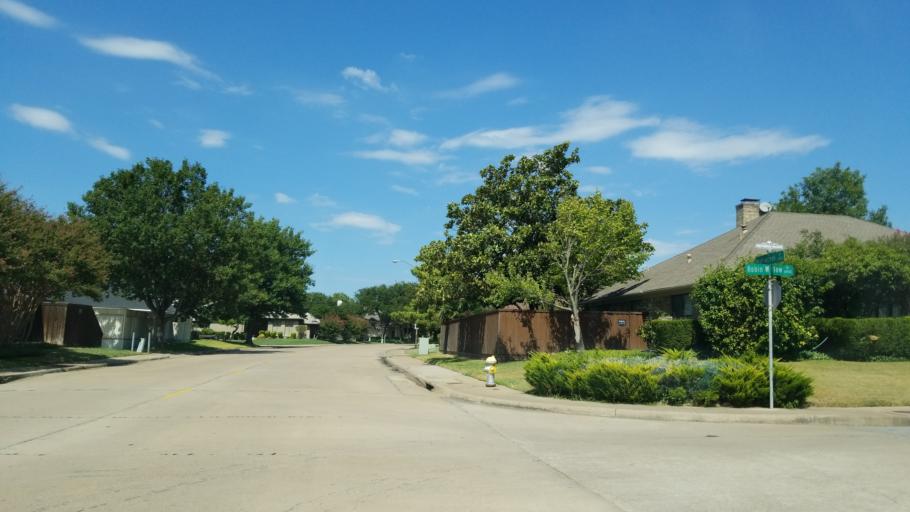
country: US
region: Texas
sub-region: Dallas County
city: Addison
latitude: 32.9686
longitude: -96.7913
